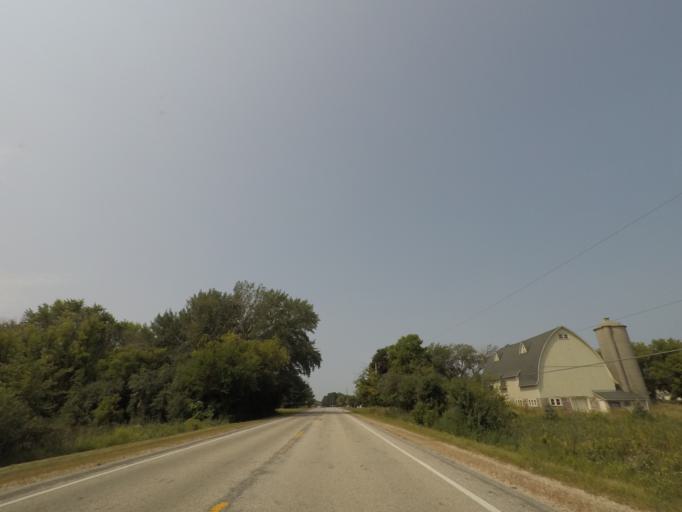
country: US
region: Wisconsin
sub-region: Waukesha County
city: Oconomowoc
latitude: 43.0609
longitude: -88.5151
